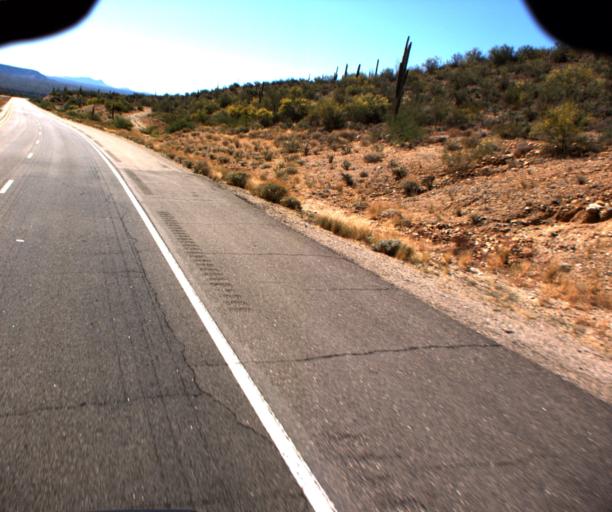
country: US
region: Arizona
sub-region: Yavapai County
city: Bagdad
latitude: 34.3989
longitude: -113.2172
